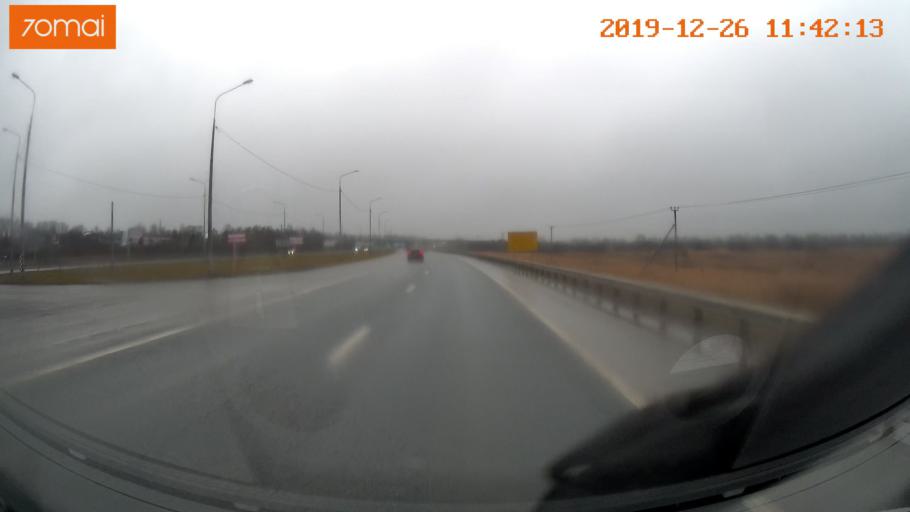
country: RU
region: Vologda
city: Sheksna
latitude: 59.2119
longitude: 38.5278
